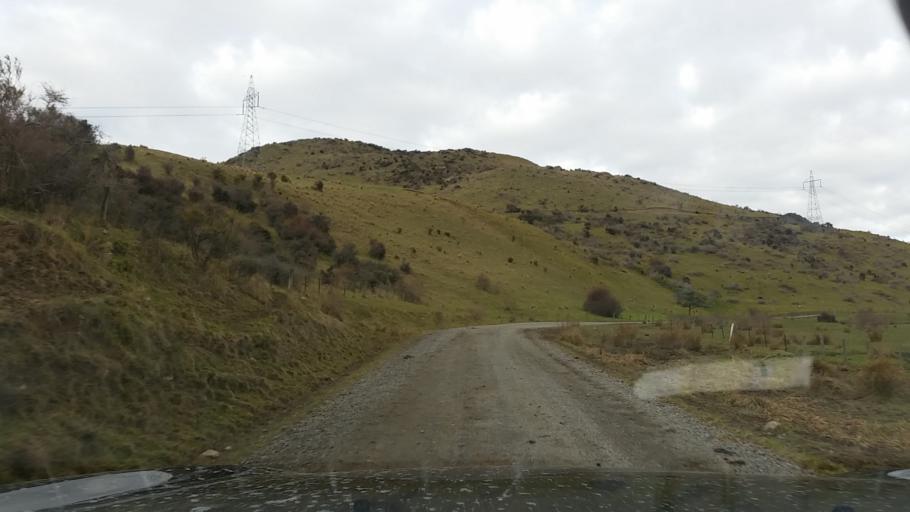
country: NZ
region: Canterbury
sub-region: Kaikoura District
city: Kaikoura
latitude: -41.9085
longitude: 173.5698
